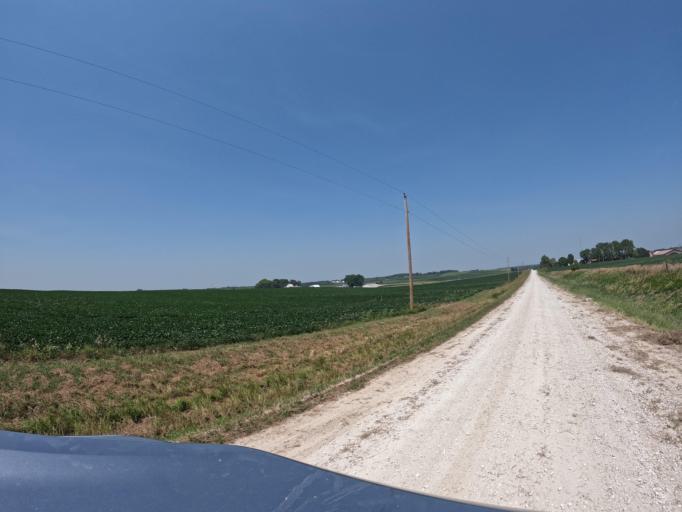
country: US
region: Iowa
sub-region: Keokuk County
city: Sigourney
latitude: 41.2837
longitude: -92.2095
